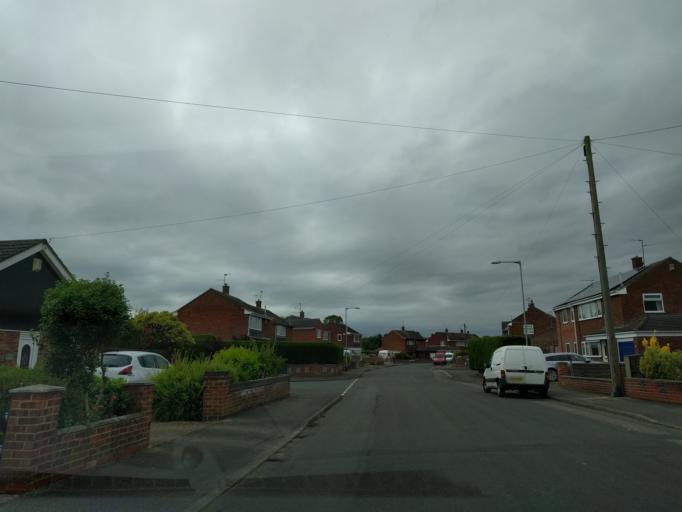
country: GB
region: England
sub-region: Nottinghamshire
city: Newark on Trent
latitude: 53.0514
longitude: -0.7848
